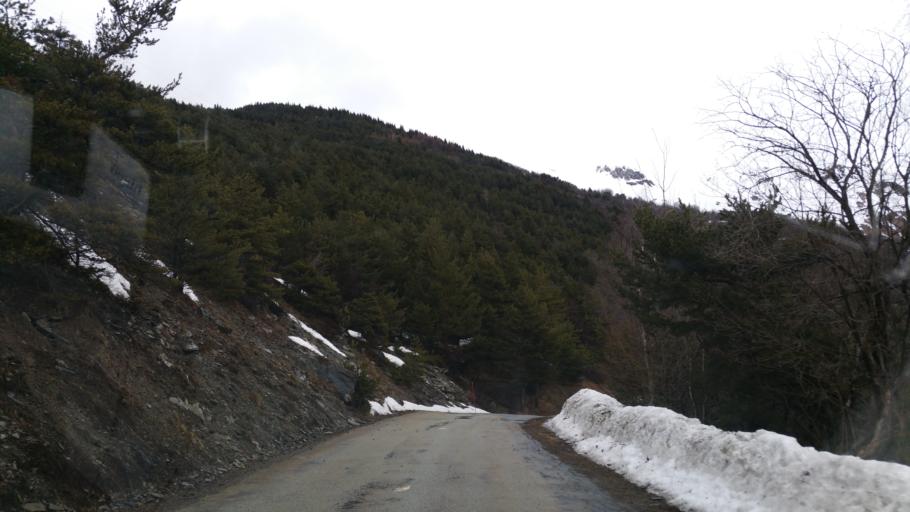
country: FR
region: Rhone-Alpes
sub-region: Departement de la Savoie
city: Villargondran
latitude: 45.2755
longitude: 6.3936
